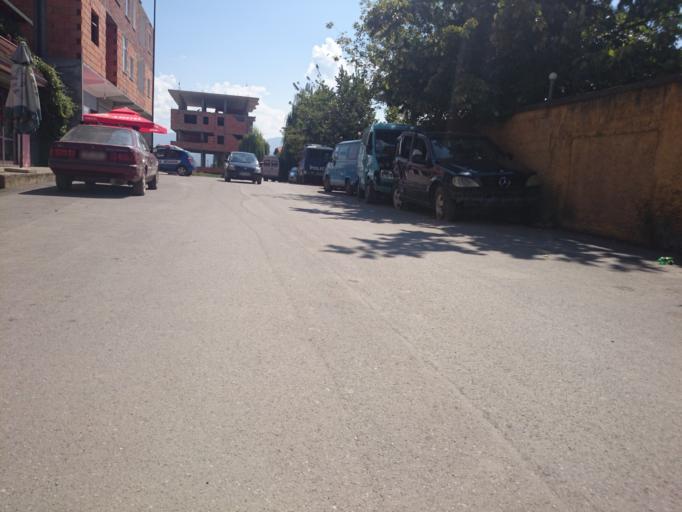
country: AL
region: Diber
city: Peshkopi
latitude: 41.6825
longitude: 20.4247
